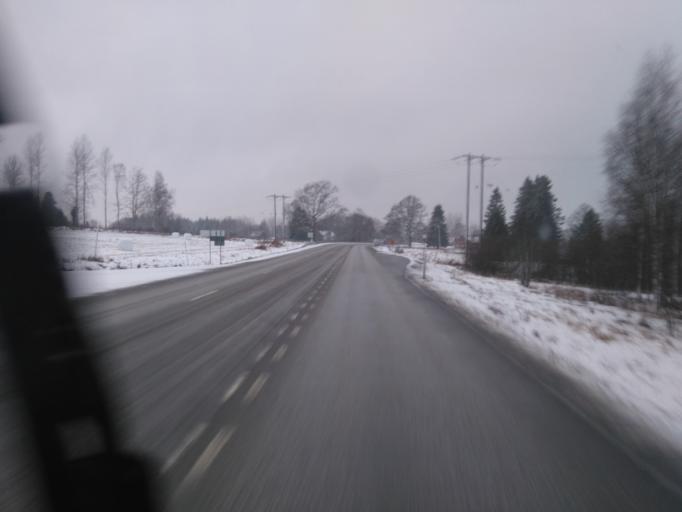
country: SE
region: Joenkoeping
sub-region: Eksjo Kommun
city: Eksjoe
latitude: 57.6390
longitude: 15.0882
